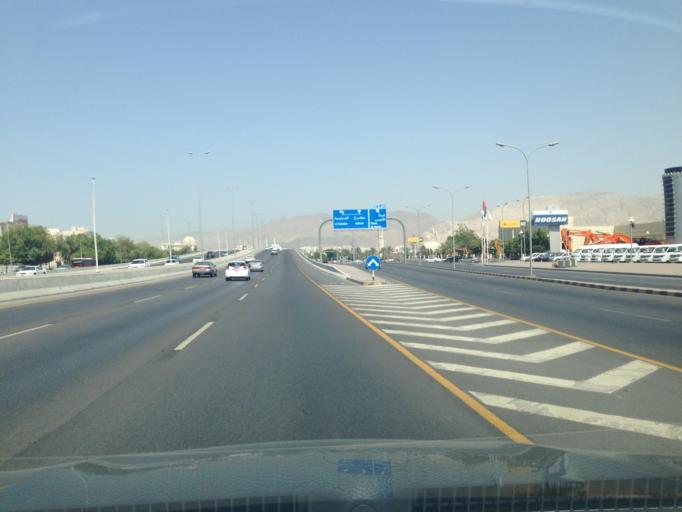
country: OM
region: Muhafazat Masqat
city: Bawshar
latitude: 23.5892
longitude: 58.3794
